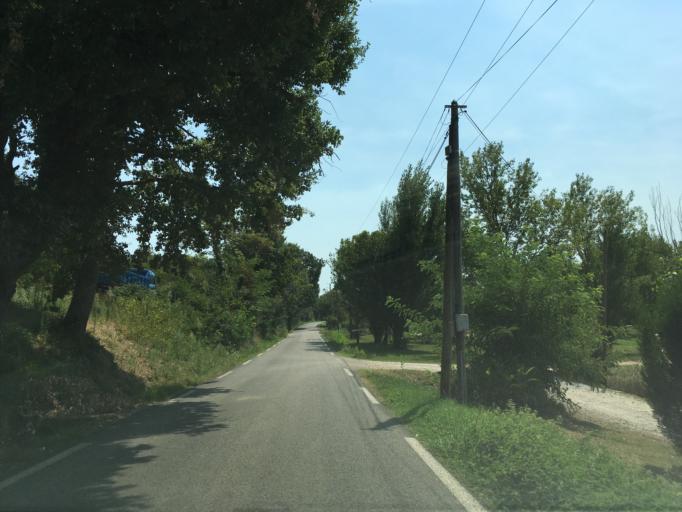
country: FR
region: Midi-Pyrenees
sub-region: Departement du Tarn-et-Garonne
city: Saint-Nauphary
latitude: 43.9734
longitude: 1.3948
